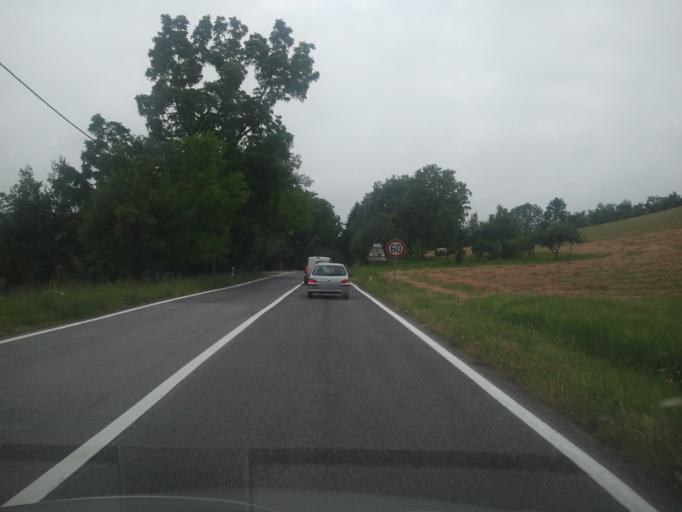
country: HR
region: Karlovacka
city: Vojnic
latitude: 45.3421
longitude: 15.6099
